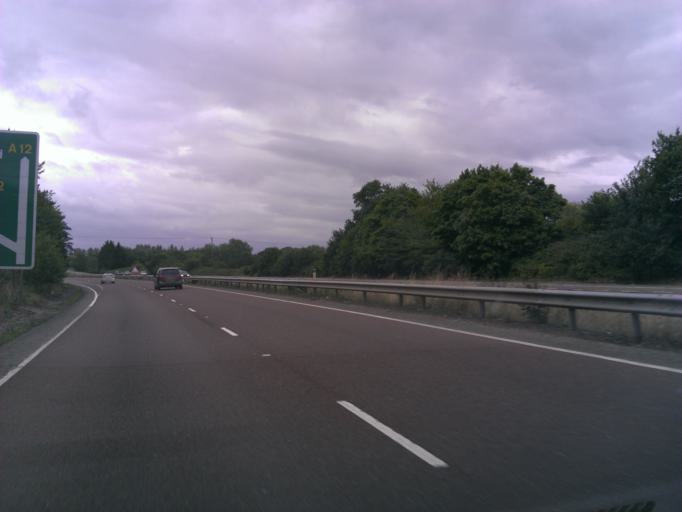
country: GB
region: England
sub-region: Essex
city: Colchester
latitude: 51.9189
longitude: 0.9414
